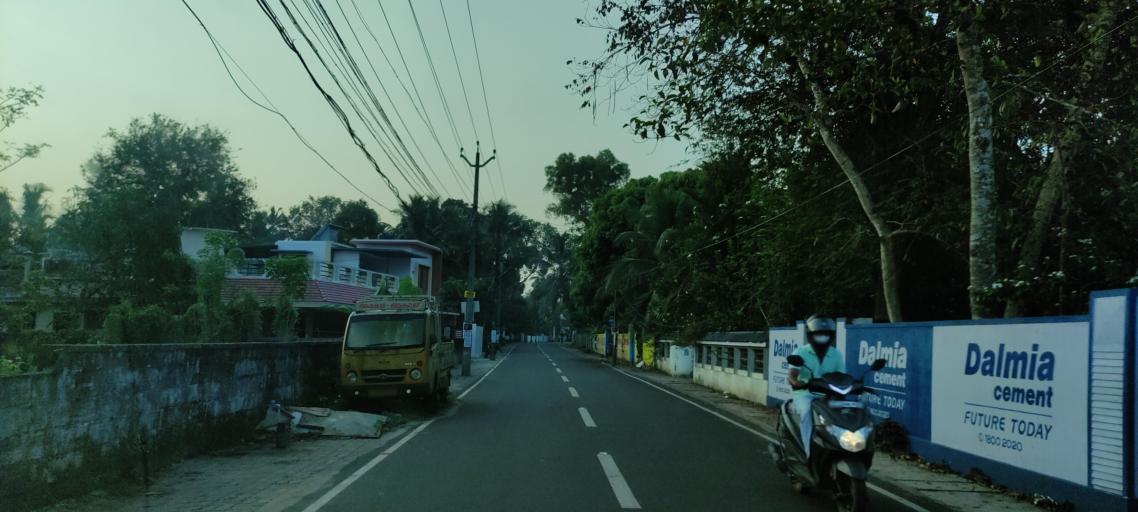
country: IN
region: Kerala
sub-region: Alappuzha
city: Alleppey
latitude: 9.4494
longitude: 76.3455
